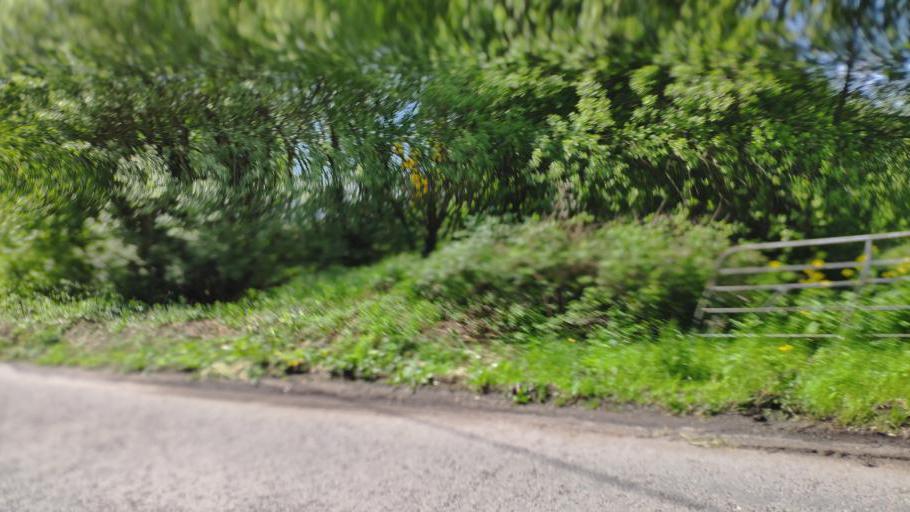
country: IE
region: Munster
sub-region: County Cork
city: Blarney
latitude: 51.9576
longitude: -8.5755
